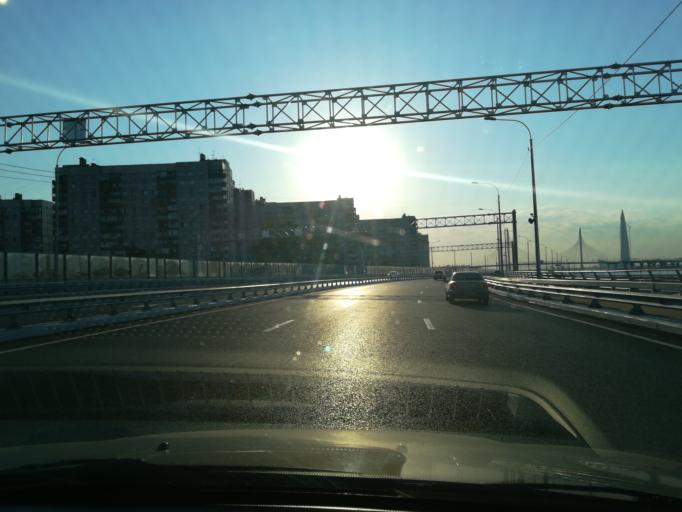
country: RU
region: St.-Petersburg
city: Vasyl'evsky Ostrov
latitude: 59.9581
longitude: 30.2386
